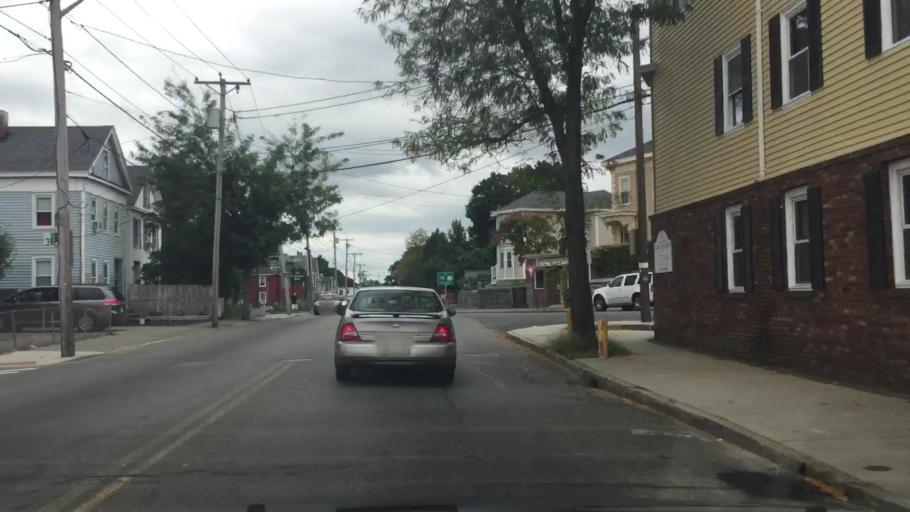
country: US
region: Massachusetts
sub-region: Middlesex County
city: Lowell
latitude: 42.6370
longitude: -71.3089
